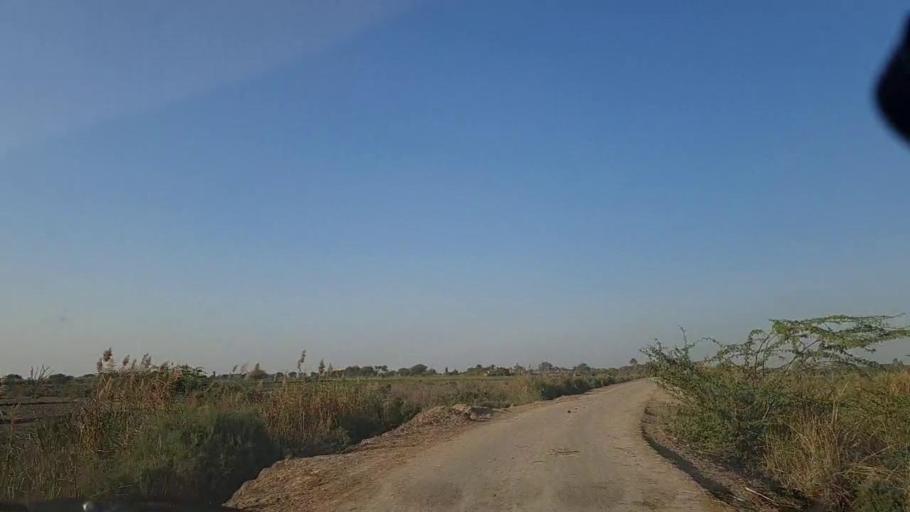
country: PK
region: Sindh
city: Berani
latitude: 25.6707
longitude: 68.9146
